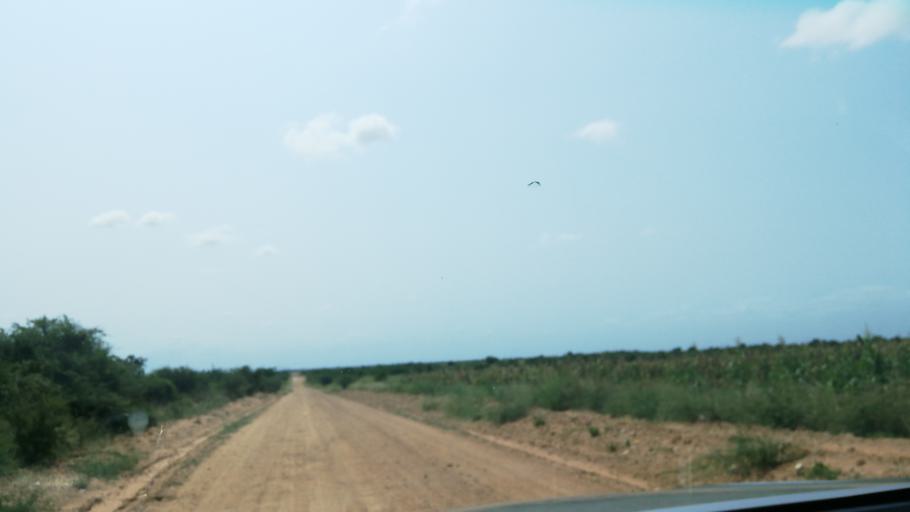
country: MZ
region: Maputo
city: Matola
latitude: -26.0825
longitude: 32.3914
